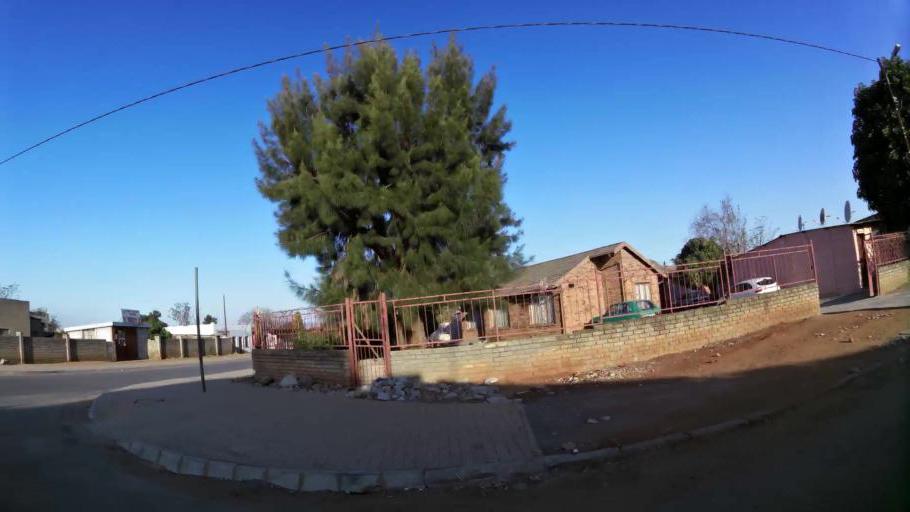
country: ZA
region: North-West
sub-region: Bojanala Platinum District Municipality
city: Rustenburg
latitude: -25.6421
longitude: 27.2173
